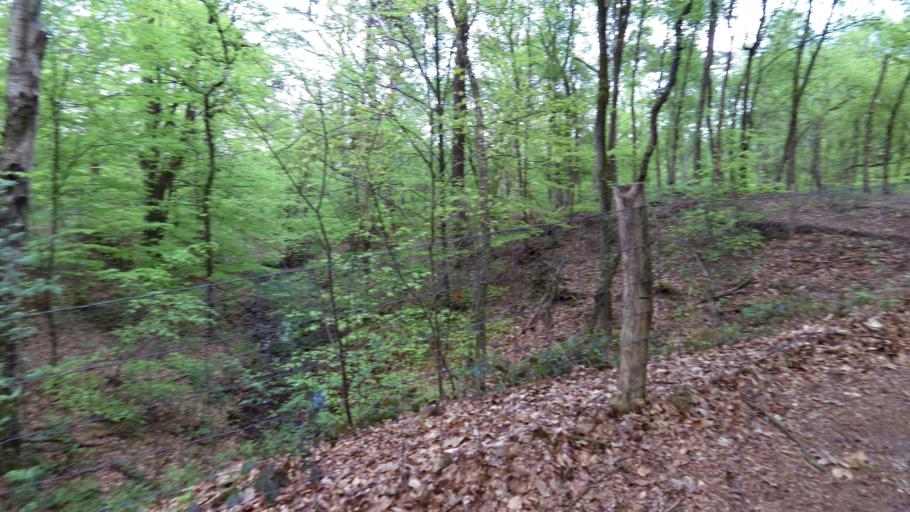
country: NL
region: Gelderland
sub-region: Gemeente Brummen
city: Eerbeek
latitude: 52.0821
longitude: 6.0538
